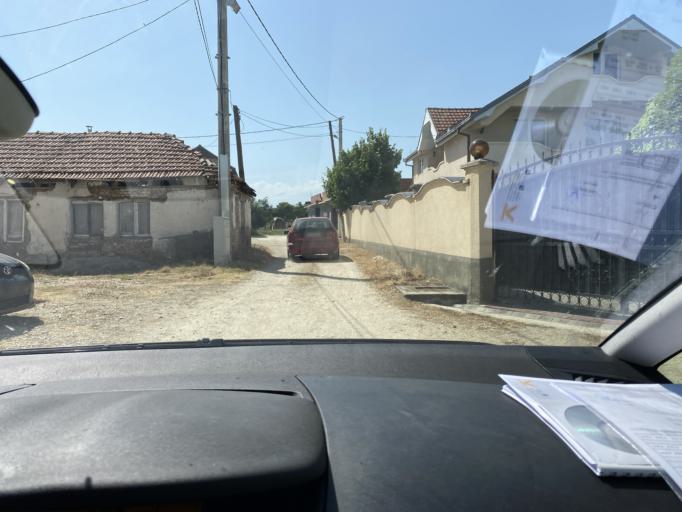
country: MK
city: Creshevo
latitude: 42.0217
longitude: 21.5057
